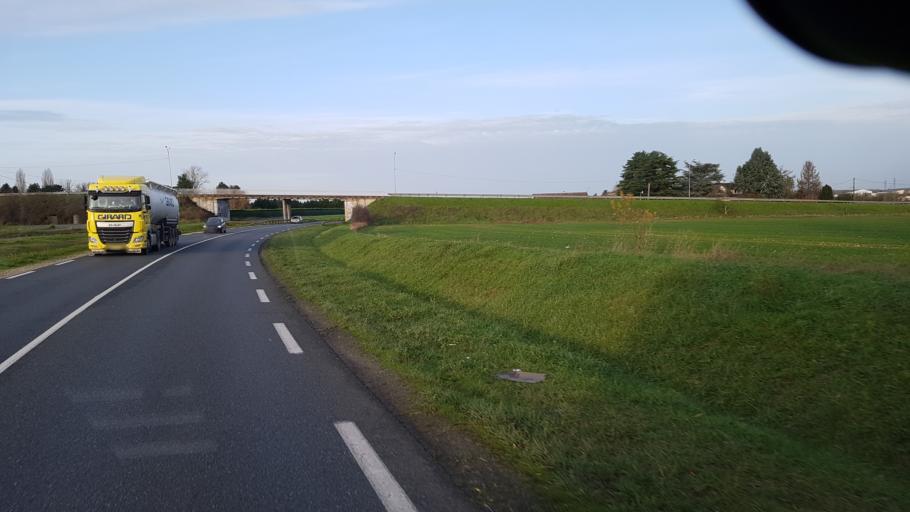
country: FR
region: Centre
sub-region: Departement de l'Indre
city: Chateauroux
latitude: 46.7860
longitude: 1.6793
